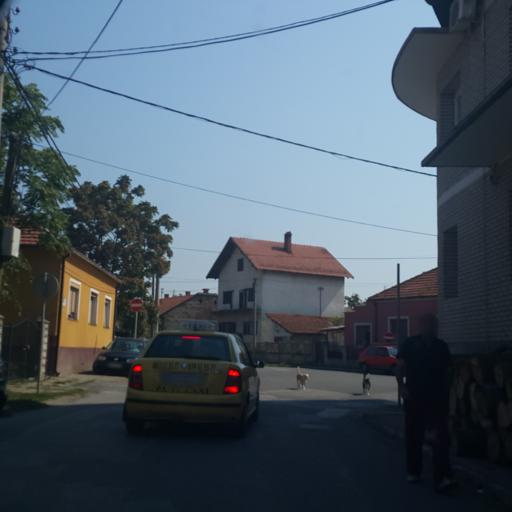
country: RS
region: Central Serbia
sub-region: Zajecarski Okrug
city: Zajecar
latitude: 43.9053
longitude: 22.2814
